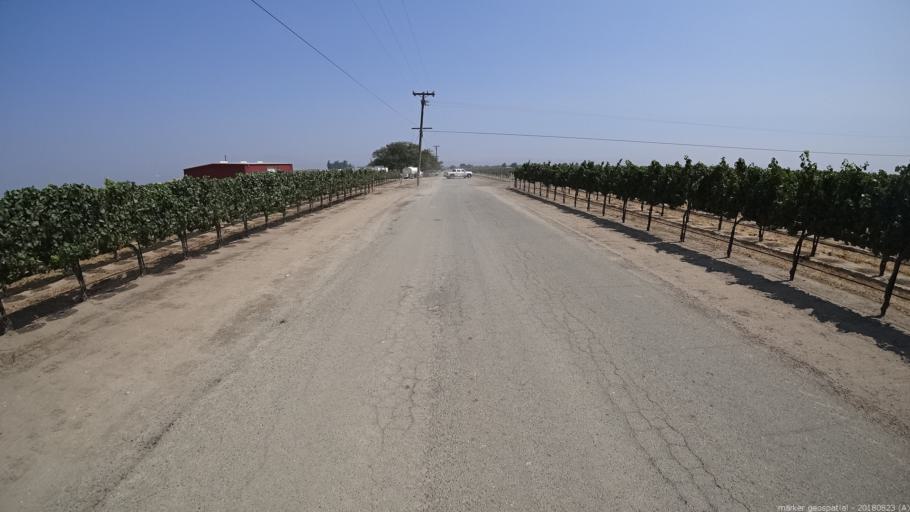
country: US
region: California
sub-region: Monterey County
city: Greenfield
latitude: 36.3037
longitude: -121.2751
